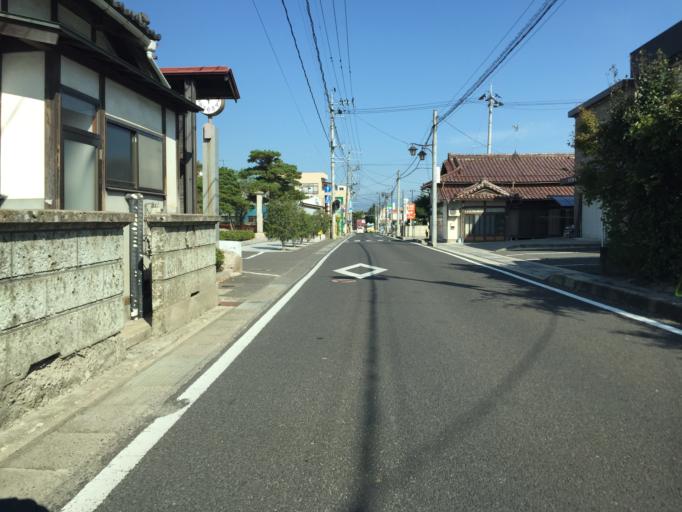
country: JP
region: Fukushima
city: Fukushima-shi
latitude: 37.7277
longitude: 140.4384
